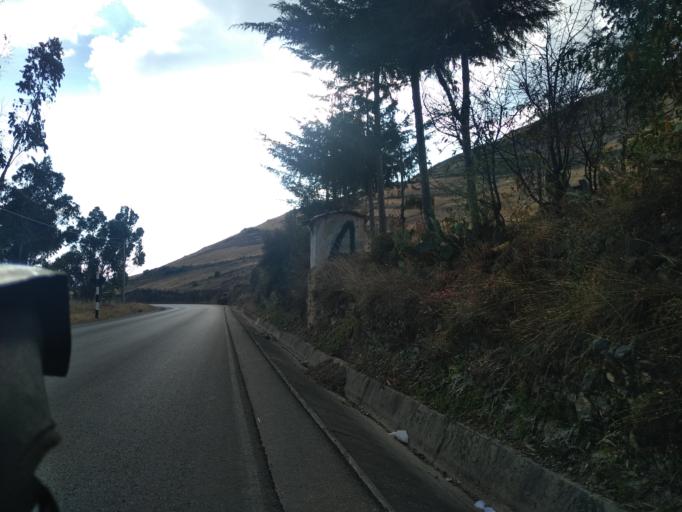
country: PE
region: Cajamarca
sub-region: Provincia de Cajamarca
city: Llacanora
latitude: -7.1544
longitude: -78.4155
